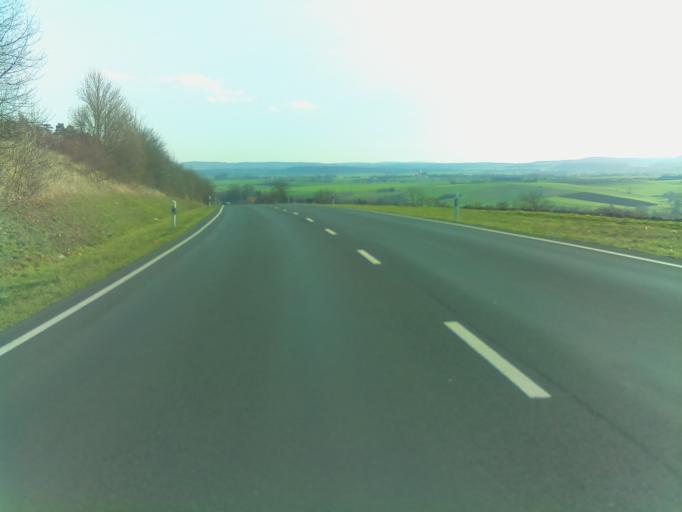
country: DE
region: Bavaria
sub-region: Regierungsbezirk Unterfranken
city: Grosseibstadt
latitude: 50.3056
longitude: 10.3951
